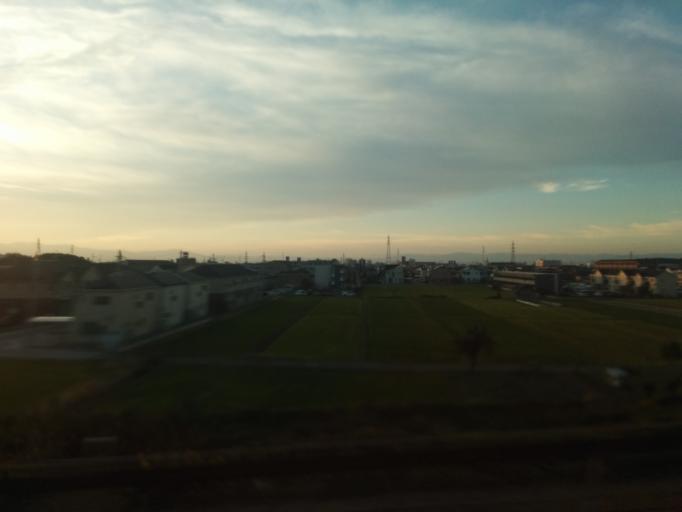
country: JP
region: Shiga Prefecture
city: Hikone
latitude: 35.2362
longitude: 136.2650
